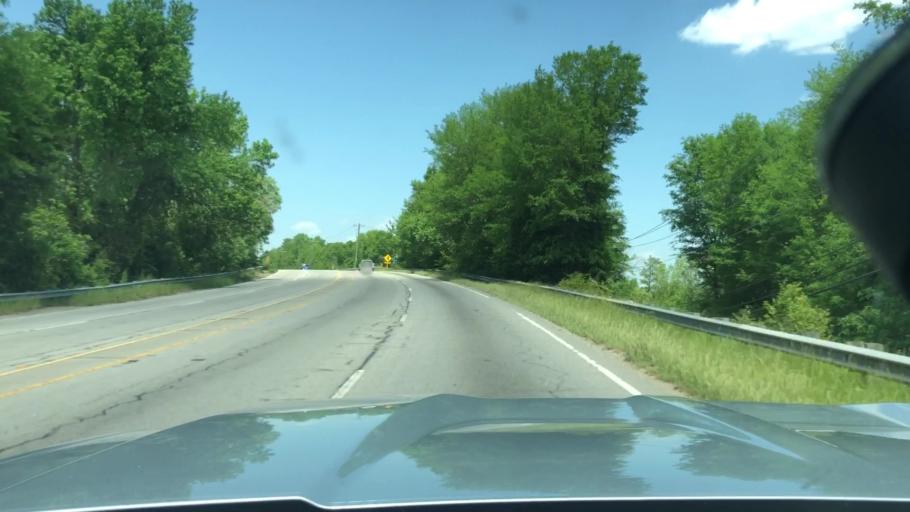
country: US
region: South Carolina
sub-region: Lexington County
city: Pineridge
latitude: 33.9078
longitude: -81.0662
